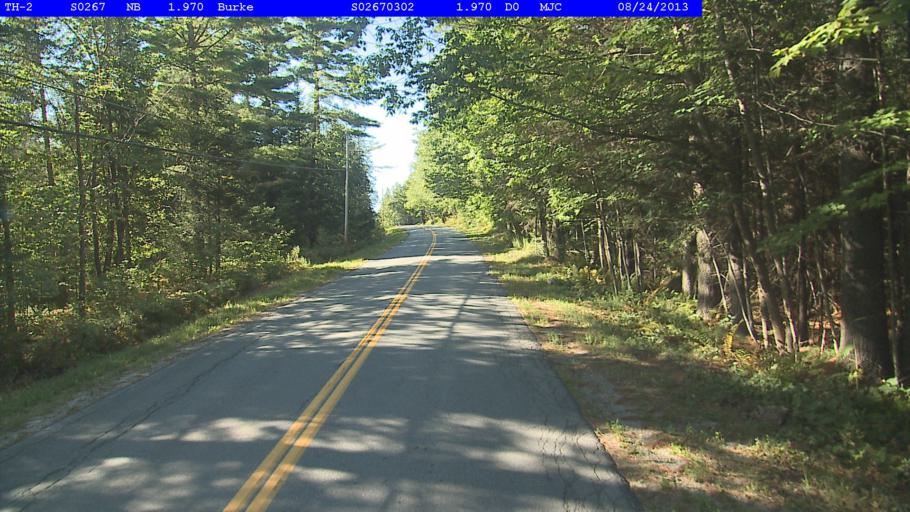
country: US
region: Vermont
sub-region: Caledonia County
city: Lyndonville
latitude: 44.6136
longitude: -71.9393
